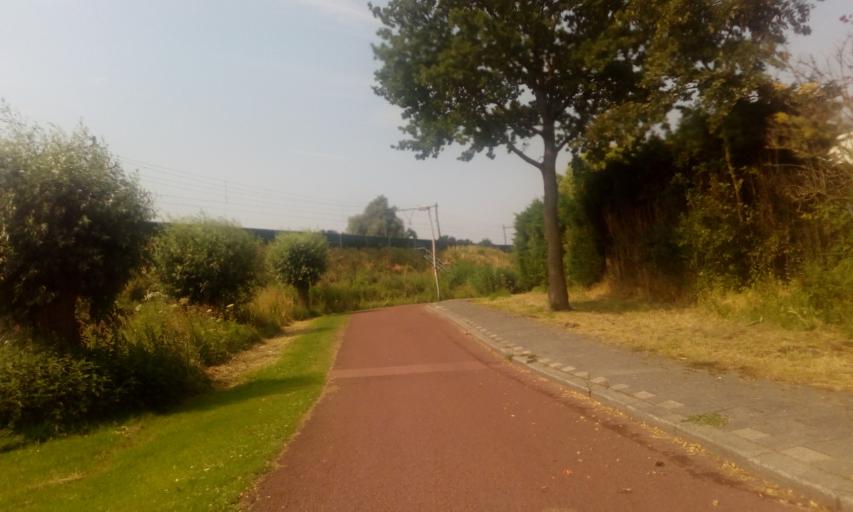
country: NL
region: South Holland
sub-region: Gemeente Capelle aan den IJssel
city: Capelle aan den IJssel
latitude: 51.9538
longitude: 4.5734
